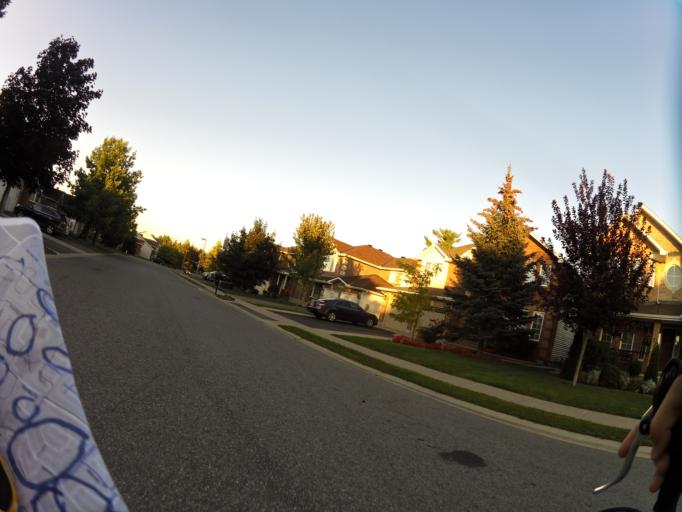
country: CA
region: Ontario
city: Bells Corners
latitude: 45.3477
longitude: -75.9403
